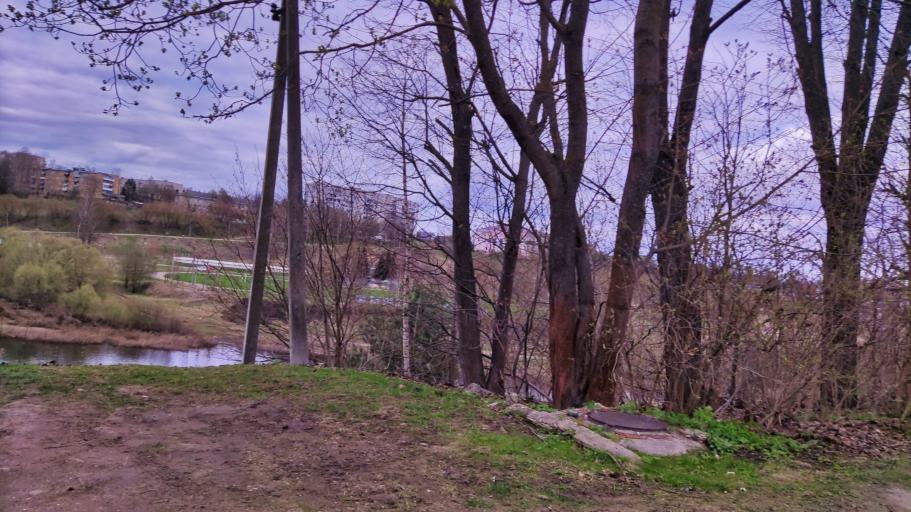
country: RU
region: Tverskaya
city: Rzhev
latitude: 56.2544
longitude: 34.3388
